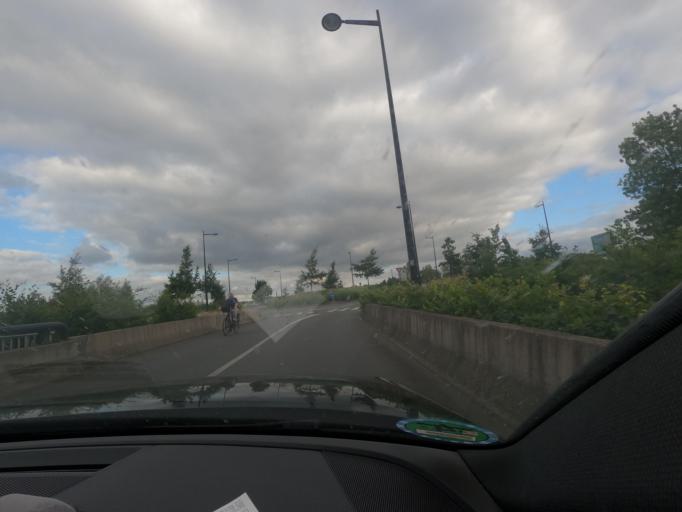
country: FR
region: Picardie
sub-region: Departement de la Somme
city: Amiens
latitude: 49.8947
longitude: 2.2769
